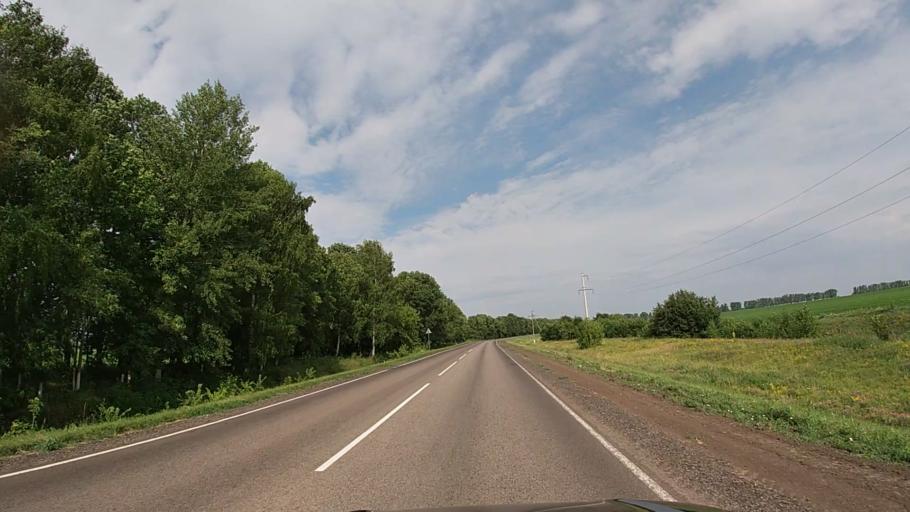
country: RU
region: Belgorod
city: Krasnaya Yaruga
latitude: 50.8016
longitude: 35.5596
